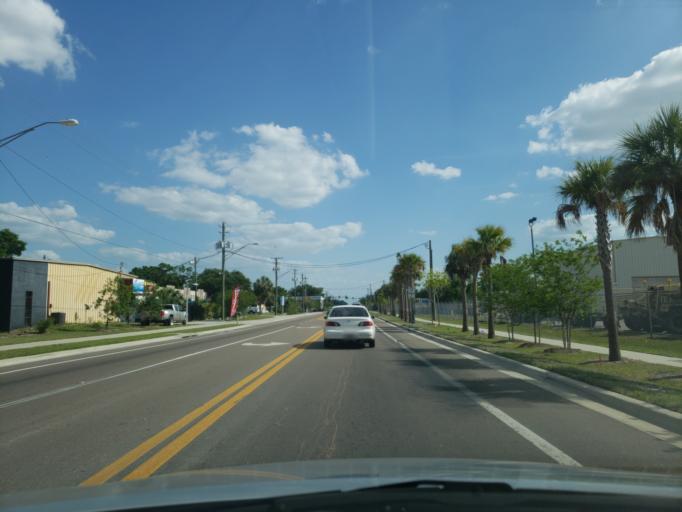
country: US
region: Florida
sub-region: Hillsborough County
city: Egypt Lake-Leto
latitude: 27.9913
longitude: -82.5135
